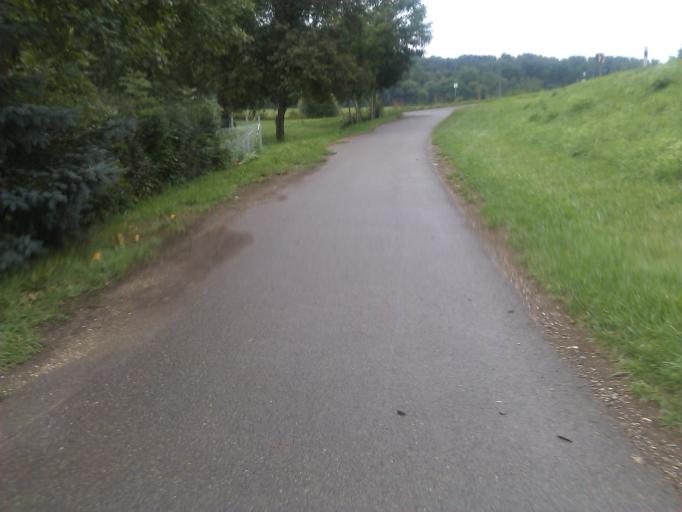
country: DE
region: Baden-Wuerttemberg
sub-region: Regierungsbezirk Stuttgart
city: Neckartenzlingen
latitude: 48.5802
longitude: 9.2323
